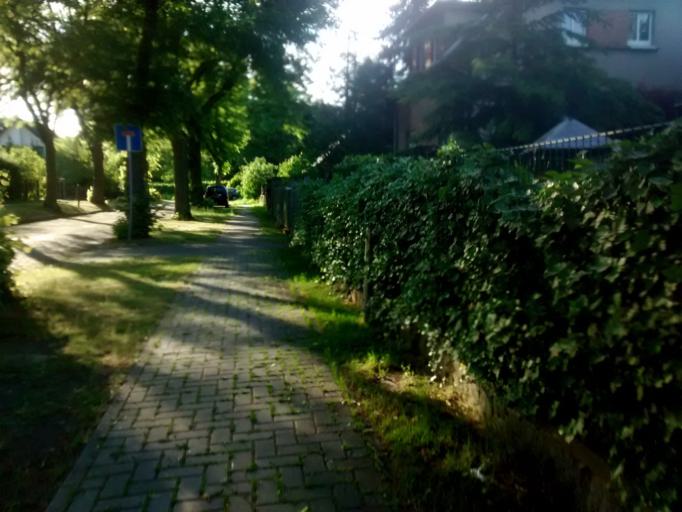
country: DE
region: Brandenburg
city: Birkenwerder
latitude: 52.6753
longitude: 13.2949
